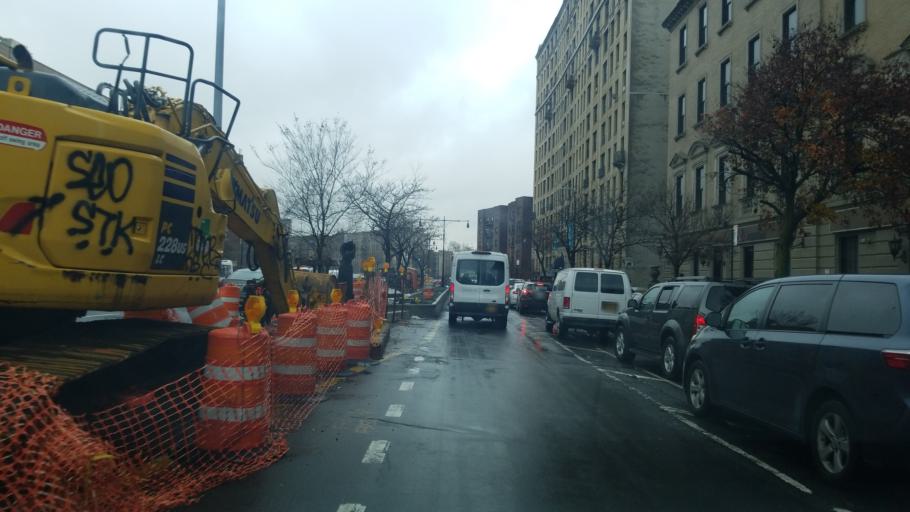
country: US
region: New York
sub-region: New York County
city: Inwood
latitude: 40.8464
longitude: -73.9097
